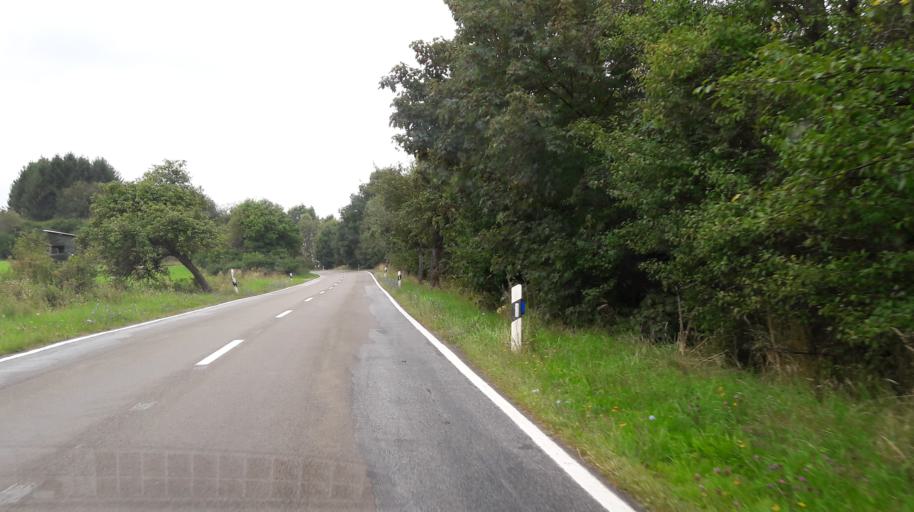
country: DE
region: Saarland
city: Namborn
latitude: 49.4839
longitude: 7.1178
